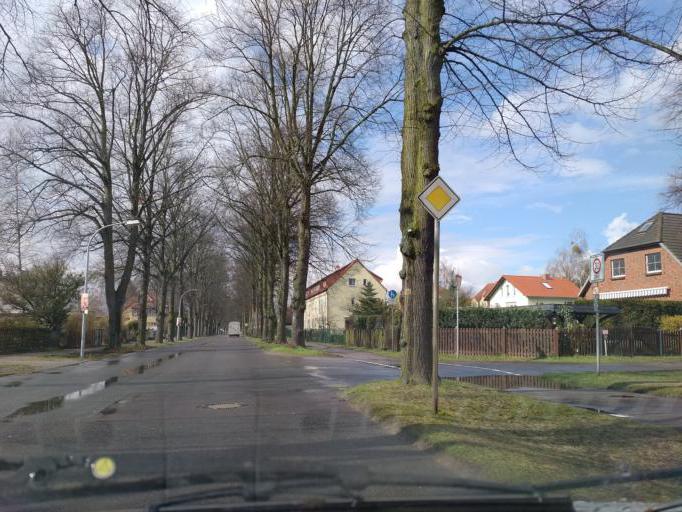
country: DE
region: Brandenburg
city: Falkensee
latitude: 52.5564
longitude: 13.1086
